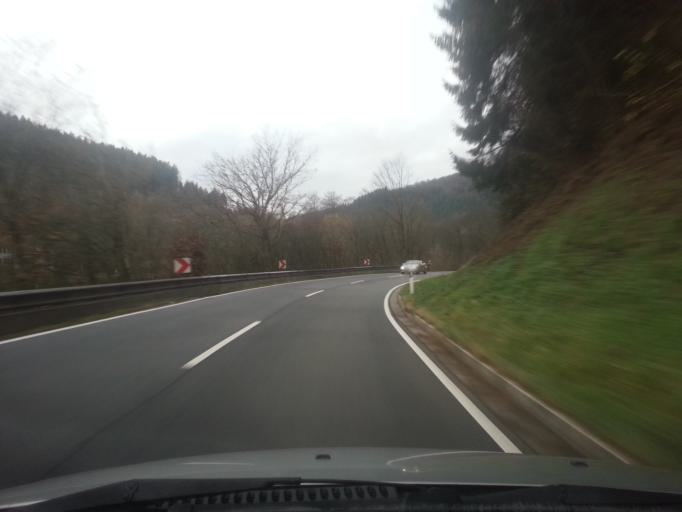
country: DE
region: Baden-Wuerttemberg
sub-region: Karlsruhe Region
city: Eberbach
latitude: 49.4859
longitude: 9.0357
